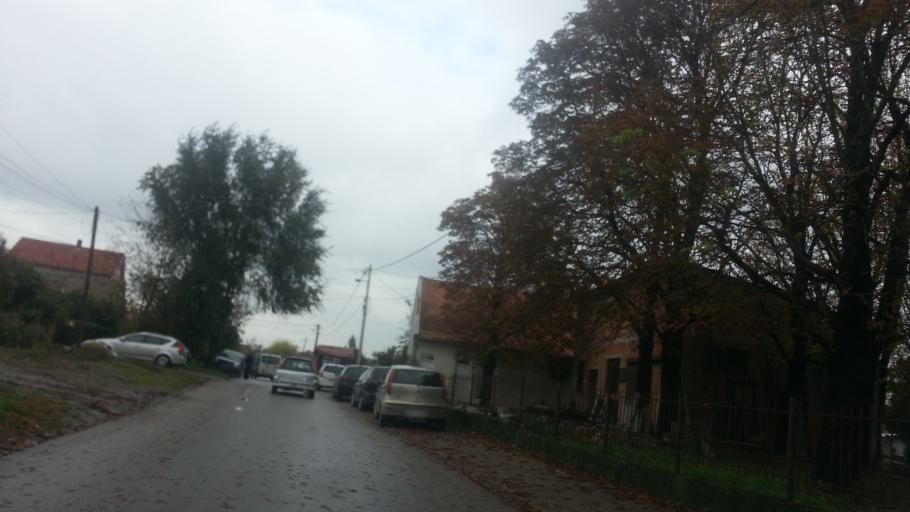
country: RS
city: Novi Banovci
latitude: 44.9068
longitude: 20.2796
